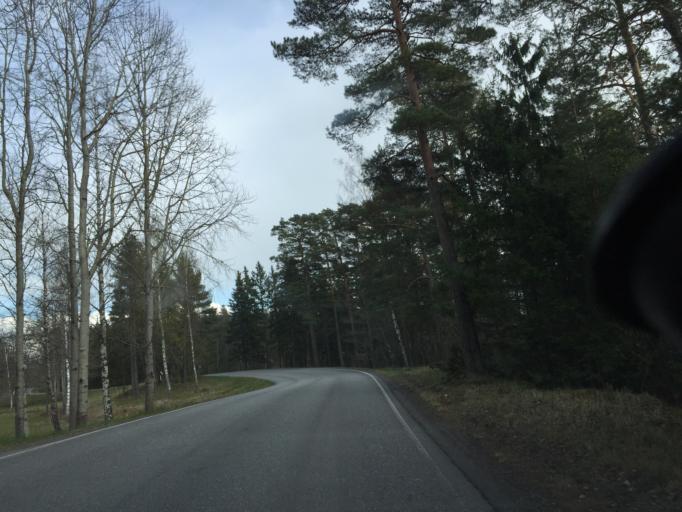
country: FI
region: Varsinais-Suomi
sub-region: Salo
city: Saerkisalo
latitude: 60.0056
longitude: 23.1023
